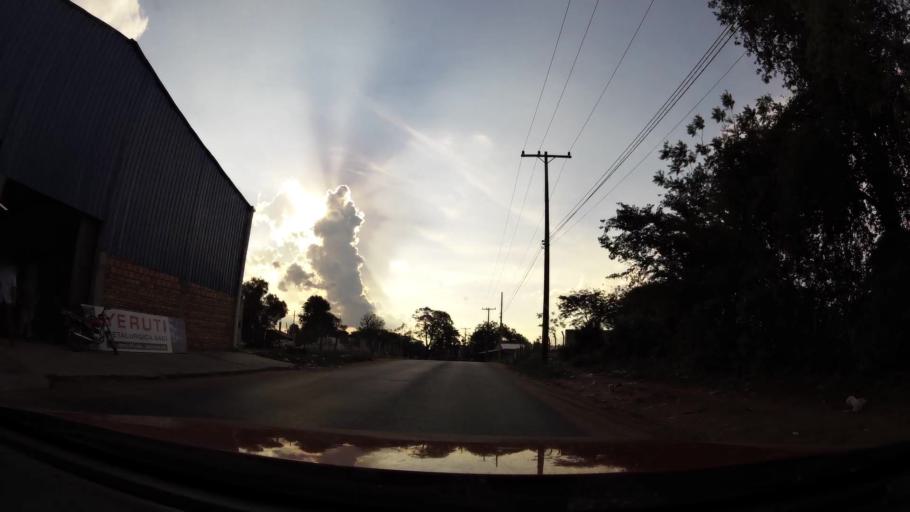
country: PY
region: Central
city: Nemby
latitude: -25.3703
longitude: -57.5255
